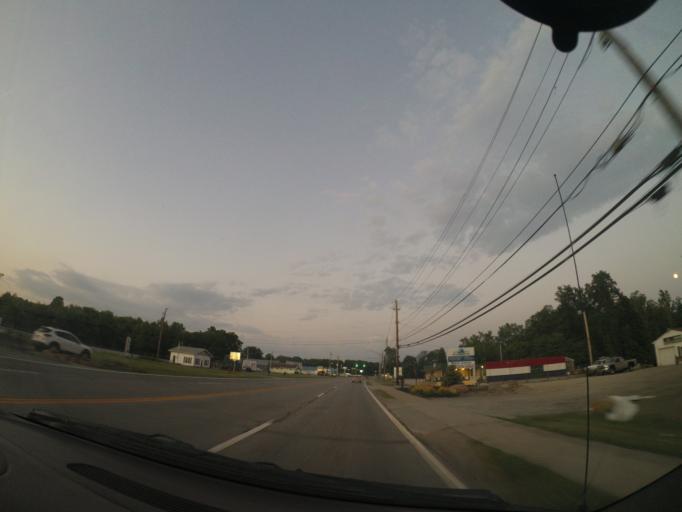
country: US
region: Ohio
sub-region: Lake County
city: North Madison
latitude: 41.8026
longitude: -81.0679
